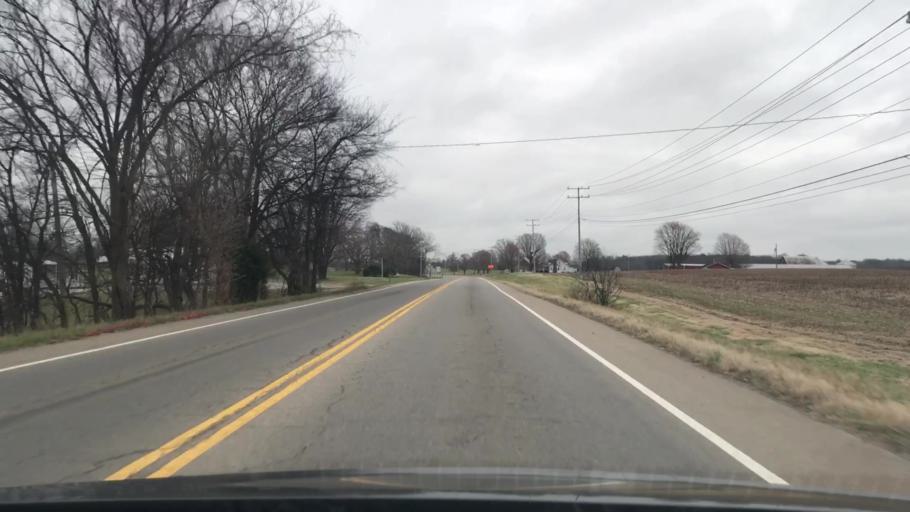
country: US
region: Kentucky
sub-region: Todd County
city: Guthrie
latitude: 36.6102
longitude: -87.2544
